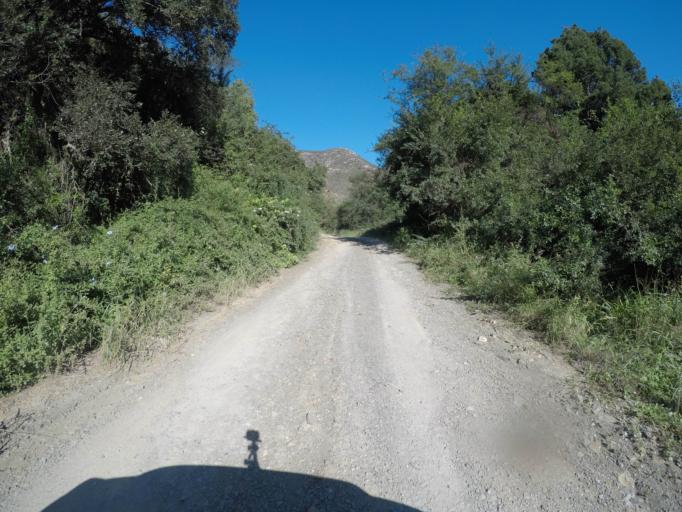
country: ZA
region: Eastern Cape
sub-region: Cacadu District Municipality
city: Kareedouw
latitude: -33.6589
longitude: 24.5284
